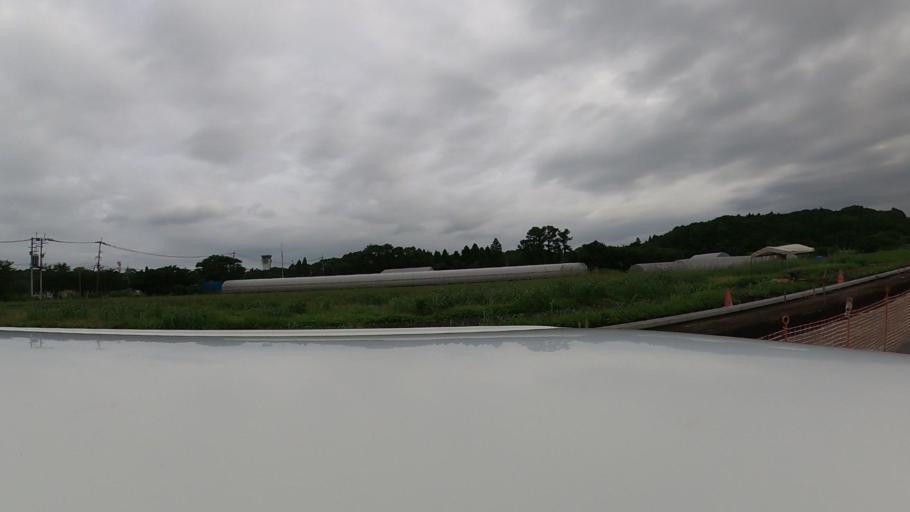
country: JP
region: Kumamoto
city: Ozu
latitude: 32.8301
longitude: 130.8603
